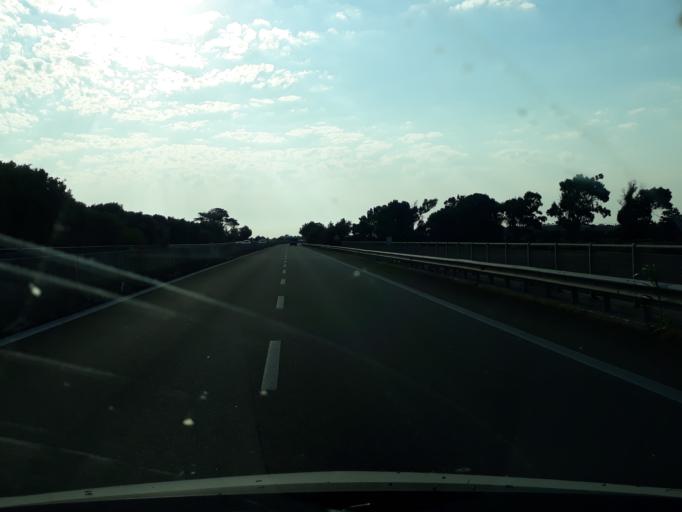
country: IT
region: Apulia
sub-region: Provincia di Brindisi
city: San Vito dei Normanni
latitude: 40.7151
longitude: 17.7772
